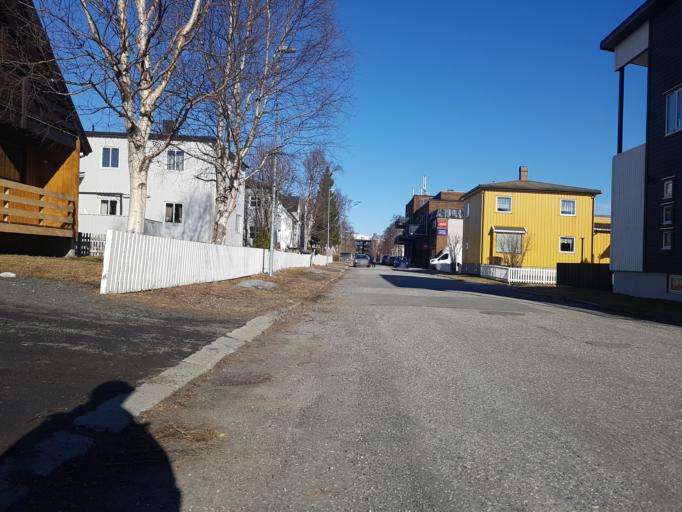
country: NO
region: Nordland
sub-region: Vefsn
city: Mosjoen
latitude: 65.8372
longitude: 13.1990
